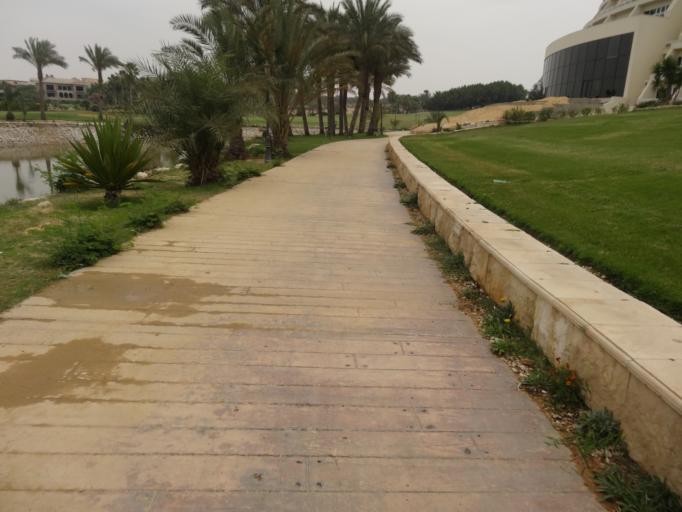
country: EG
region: Muhafazat al Qalyubiyah
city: Al Khankah
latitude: 30.0730
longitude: 31.4349
